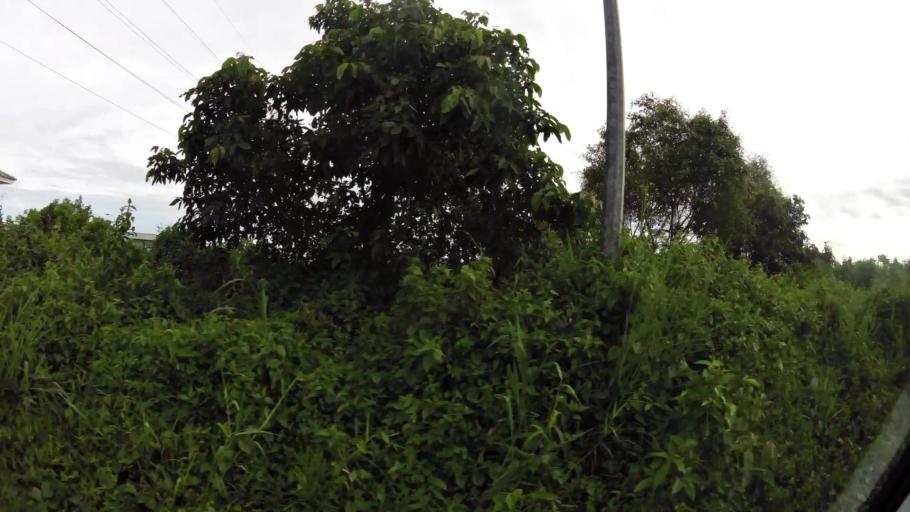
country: BN
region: Belait
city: Seria
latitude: 4.6114
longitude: 114.3409
